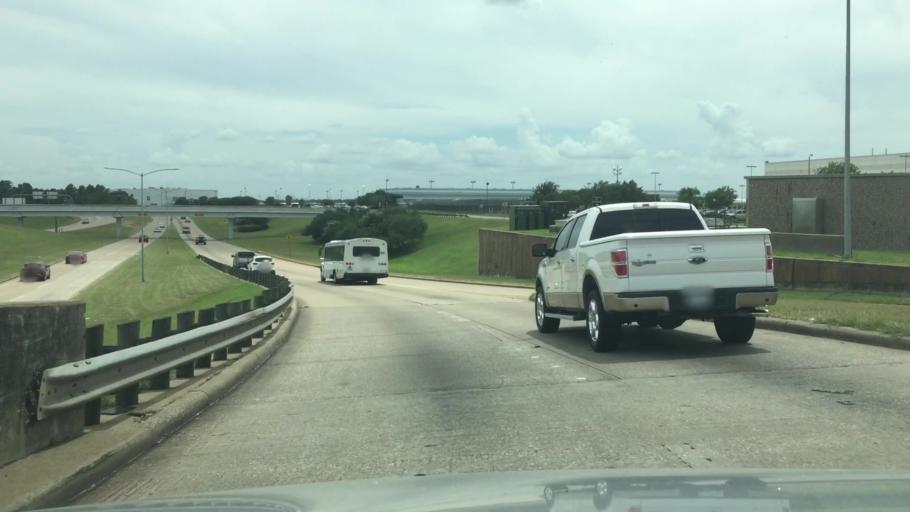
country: US
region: Texas
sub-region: Harris County
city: Aldine
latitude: 29.9807
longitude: -95.3431
